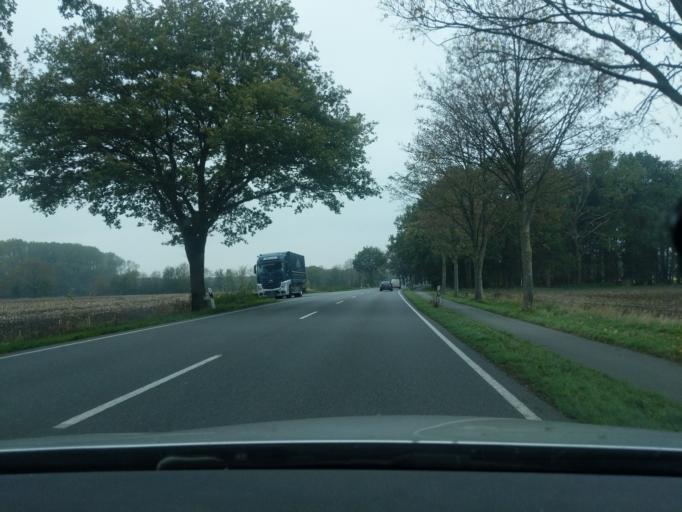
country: DE
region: Lower Saxony
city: Heinbockel
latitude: 53.5951
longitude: 9.3309
